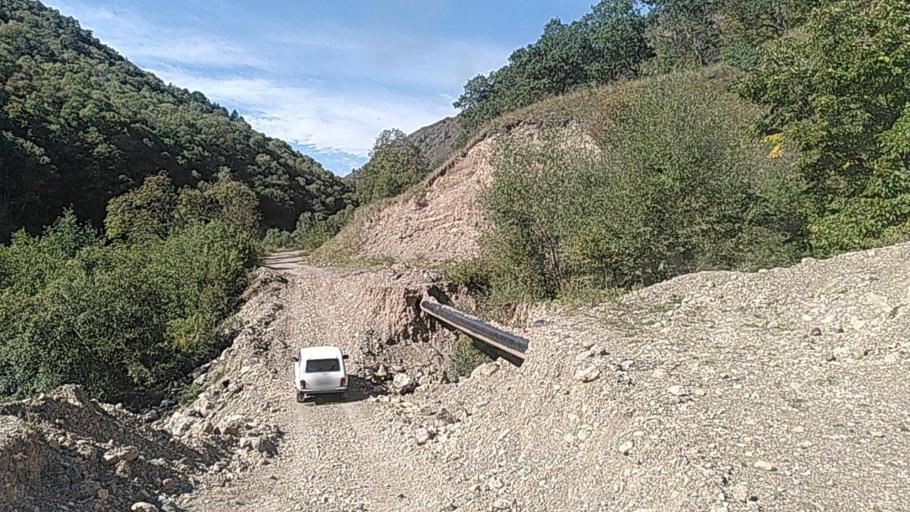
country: RU
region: Kabardino-Balkariya
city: Kamennomostskoye
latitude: 43.7230
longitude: 42.8540
